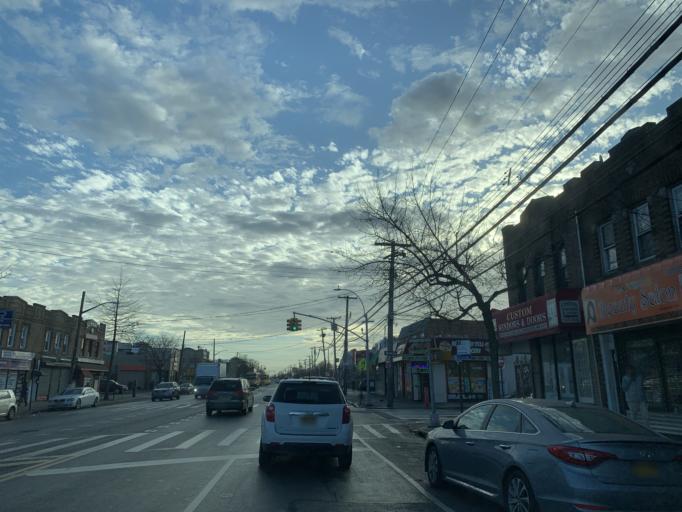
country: US
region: New York
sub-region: Queens County
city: Borough of Queens
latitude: 40.6784
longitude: -73.8325
